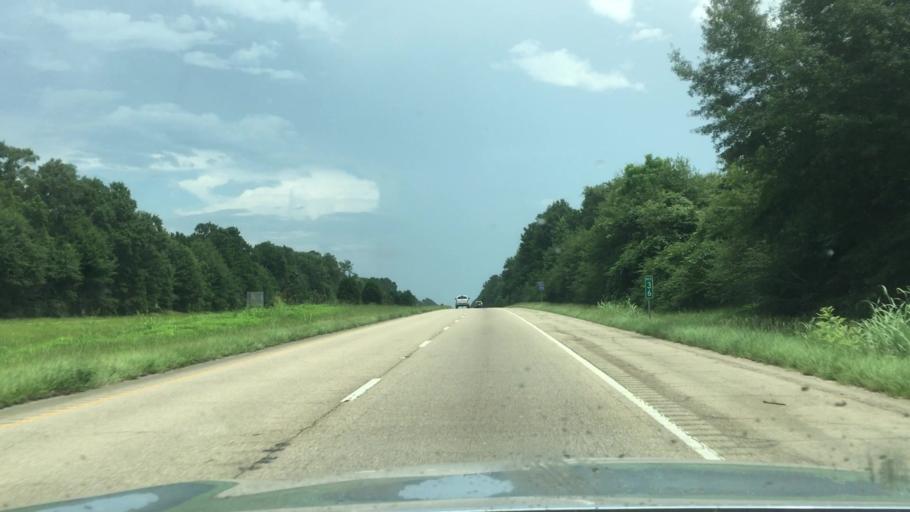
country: US
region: Mississippi
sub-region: Lamar County
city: Lumberton
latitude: 30.9277
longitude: -89.4558
